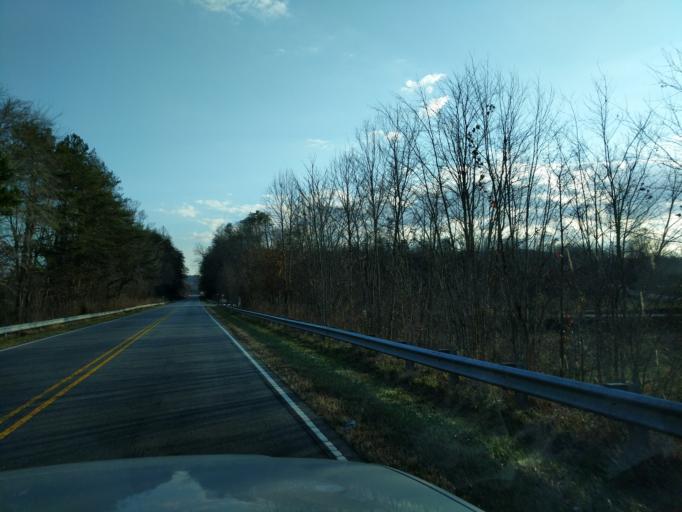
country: US
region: North Carolina
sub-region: McDowell County
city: West Marion
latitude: 35.5212
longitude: -81.9740
